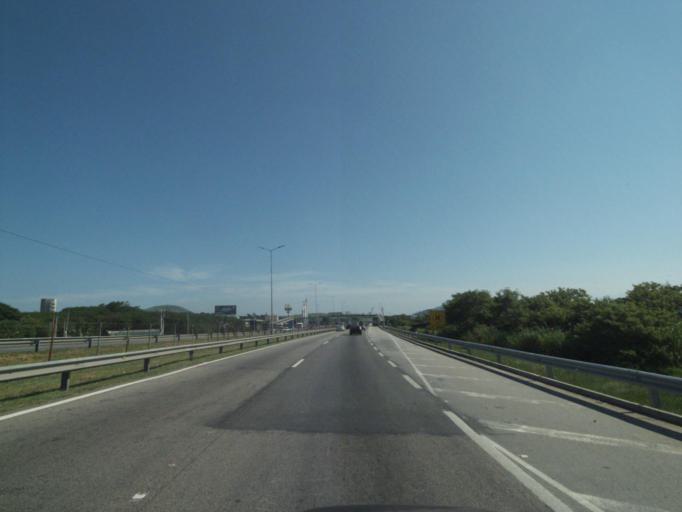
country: BR
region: Rio de Janeiro
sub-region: Niteroi
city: Niteroi
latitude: -22.8518
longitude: -43.1006
